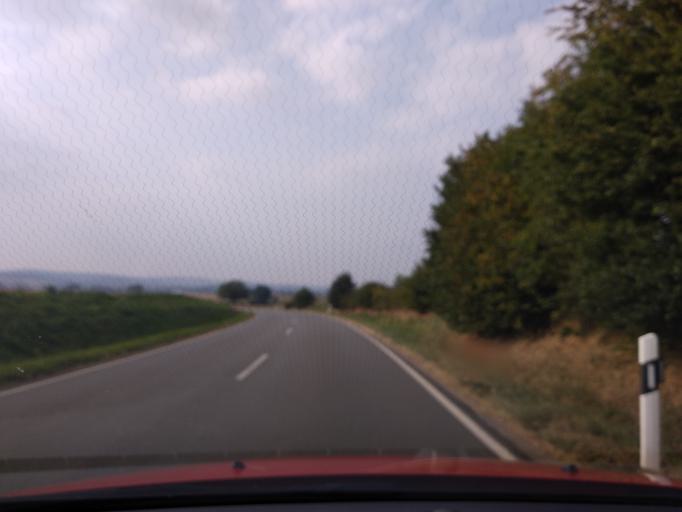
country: DE
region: Hesse
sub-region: Regierungsbezirk Kassel
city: Calden
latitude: 51.4165
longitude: 9.3462
